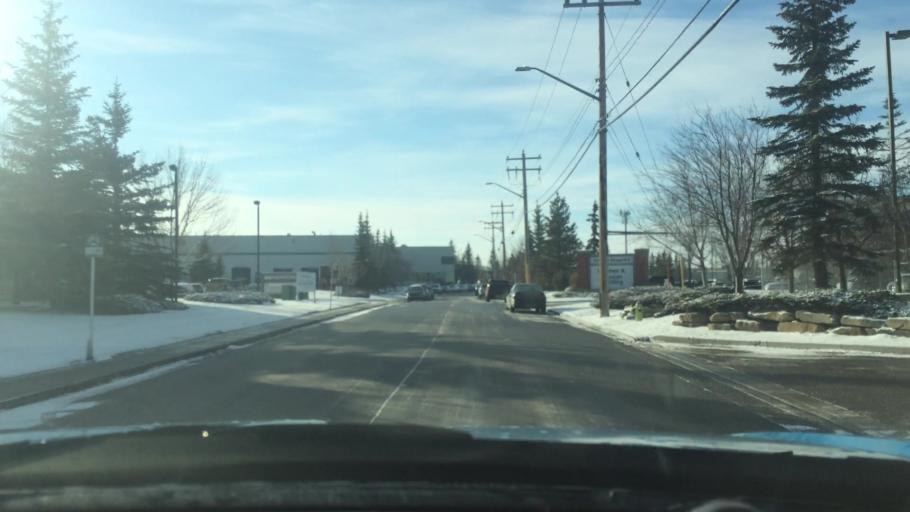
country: CA
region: Alberta
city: Calgary
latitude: 51.1202
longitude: -114.0434
